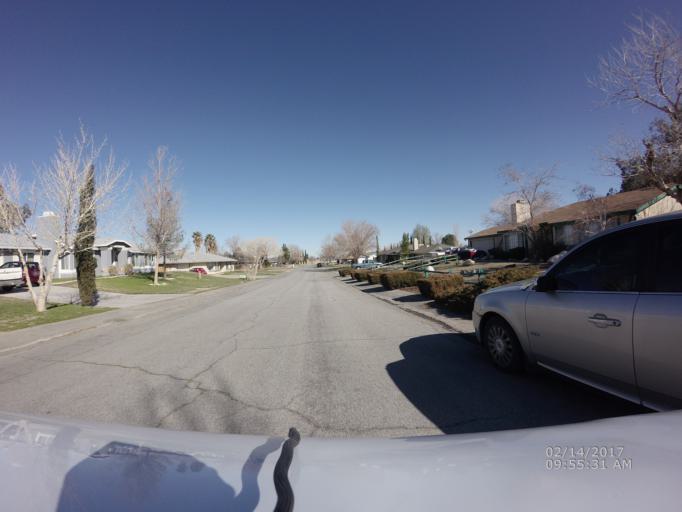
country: US
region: California
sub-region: Los Angeles County
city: Littlerock
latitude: 34.5551
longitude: -117.9613
